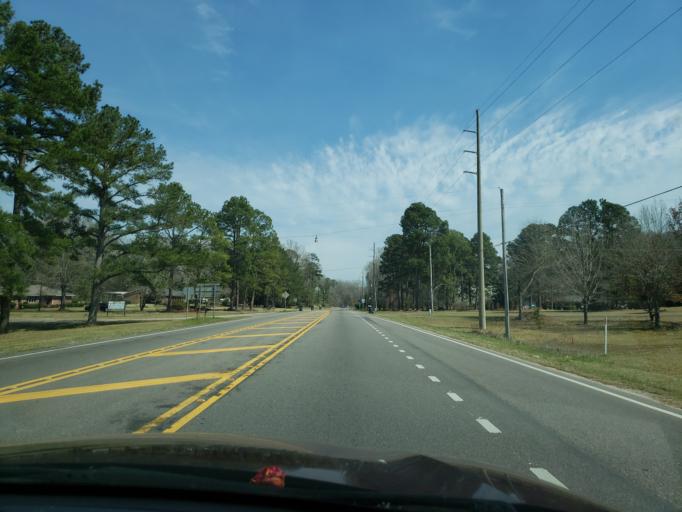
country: US
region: Alabama
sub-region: Elmore County
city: Wetumpka
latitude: 32.5520
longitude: -86.1750
